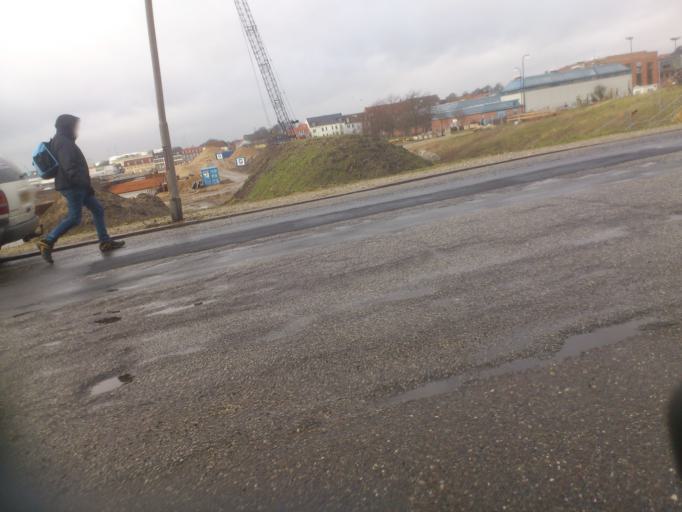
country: DK
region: South Denmark
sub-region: Fredericia Kommune
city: Fredericia
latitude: 55.5612
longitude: 9.7637
